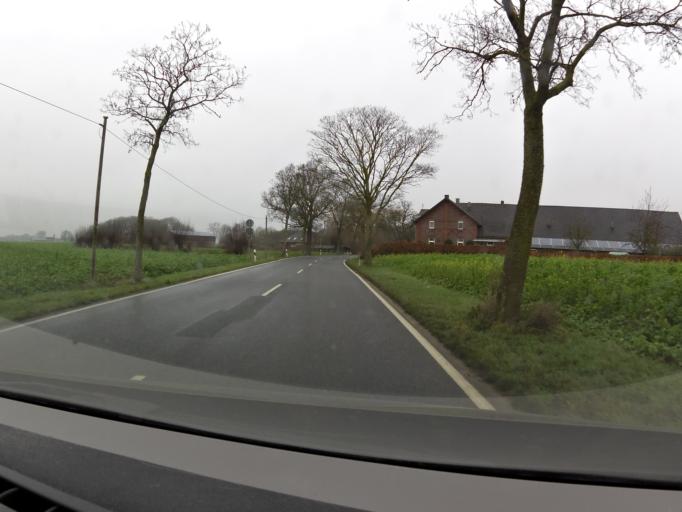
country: DE
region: North Rhine-Westphalia
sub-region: Regierungsbezirk Dusseldorf
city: Sonsbeck
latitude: 51.5793
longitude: 6.3533
